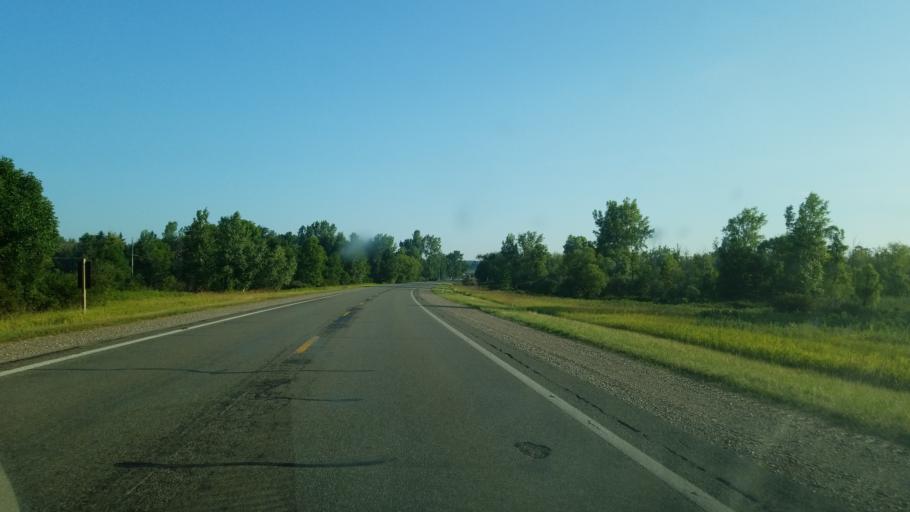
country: US
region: Michigan
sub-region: Montcalm County
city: Stanton
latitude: 43.3321
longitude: -85.0885
